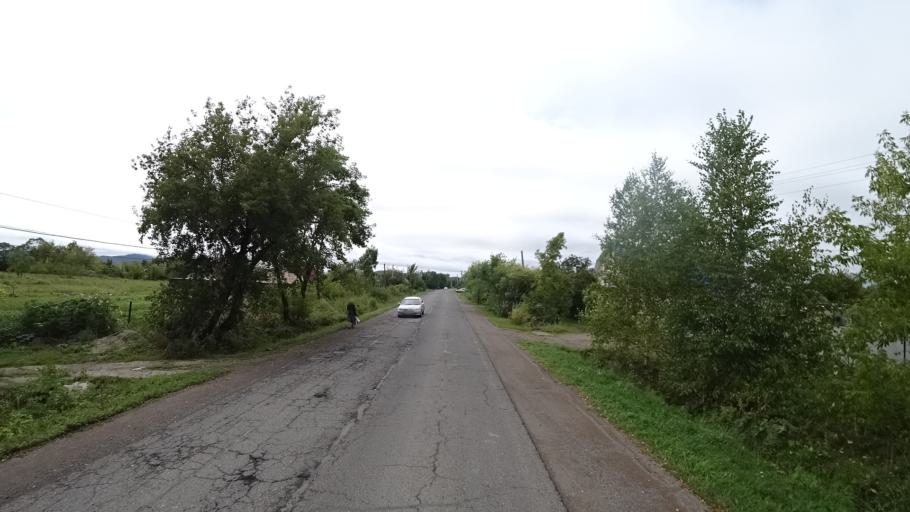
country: RU
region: Primorskiy
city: Monastyrishche
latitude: 44.2010
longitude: 132.4663
